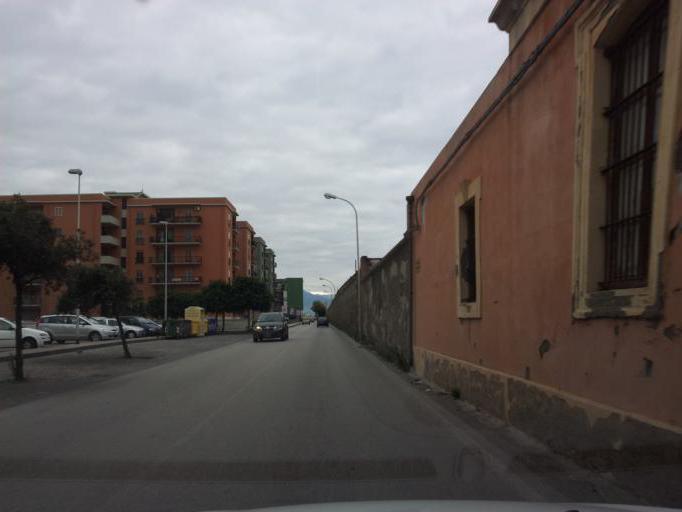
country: IT
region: Sicily
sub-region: Messina
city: Milazzo
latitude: 38.2235
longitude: 15.2351
